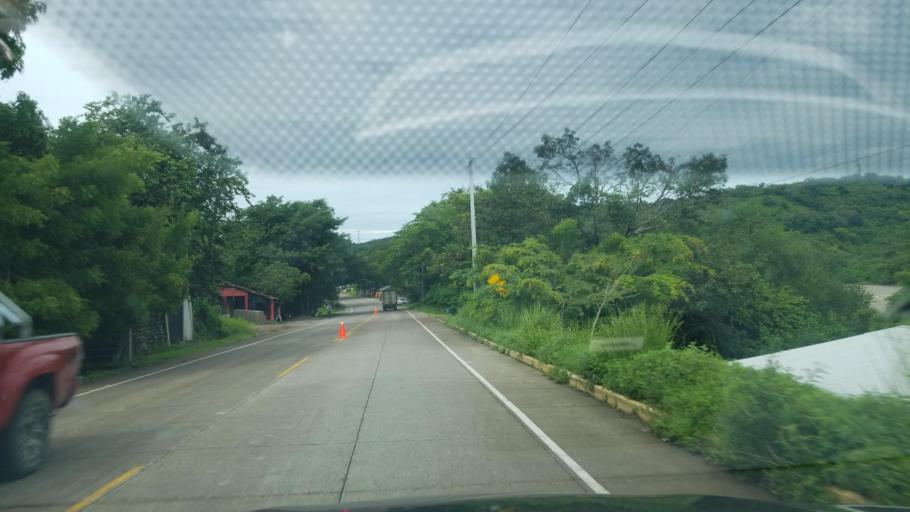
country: HN
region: Choluteca
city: Pespire
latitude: 13.6279
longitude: -87.3720
